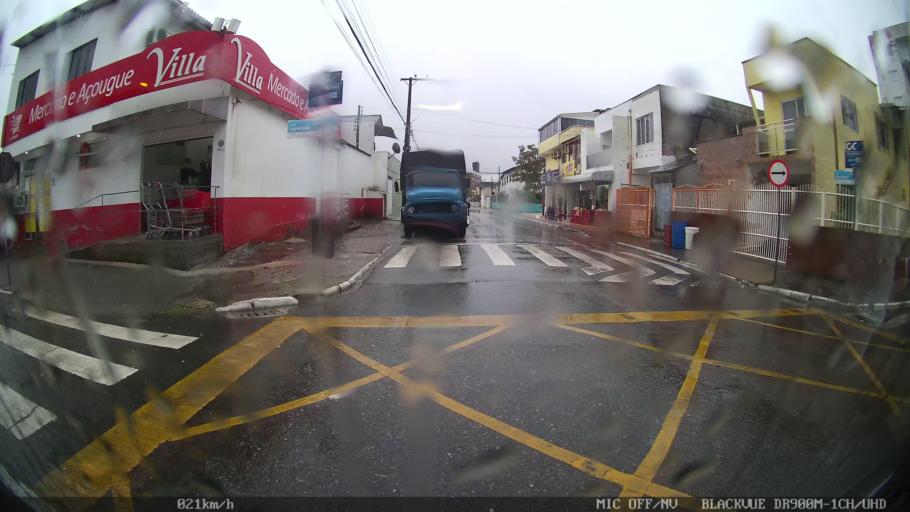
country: BR
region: Santa Catarina
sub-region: Balneario Camboriu
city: Balneario Camboriu
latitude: -27.0091
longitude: -48.6322
